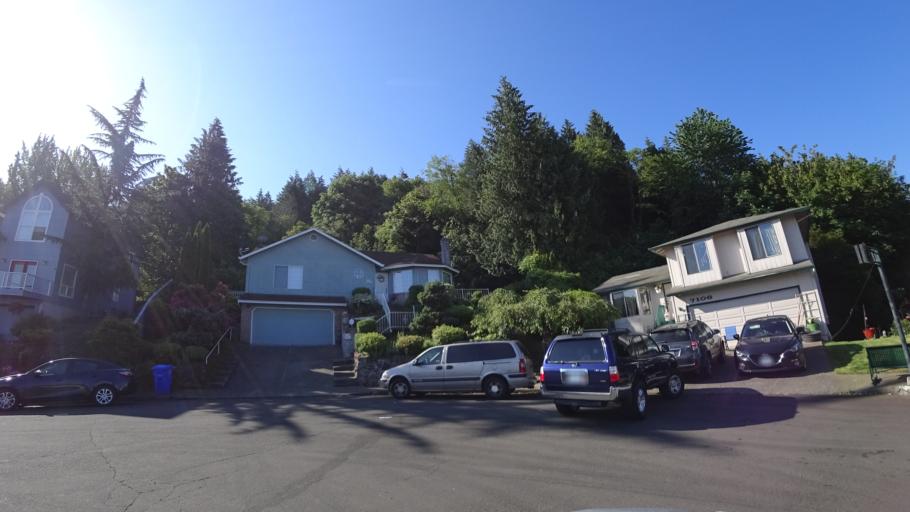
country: US
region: Oregon
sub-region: Multnomah County
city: Lents
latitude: 45.4714
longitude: -122.5446
